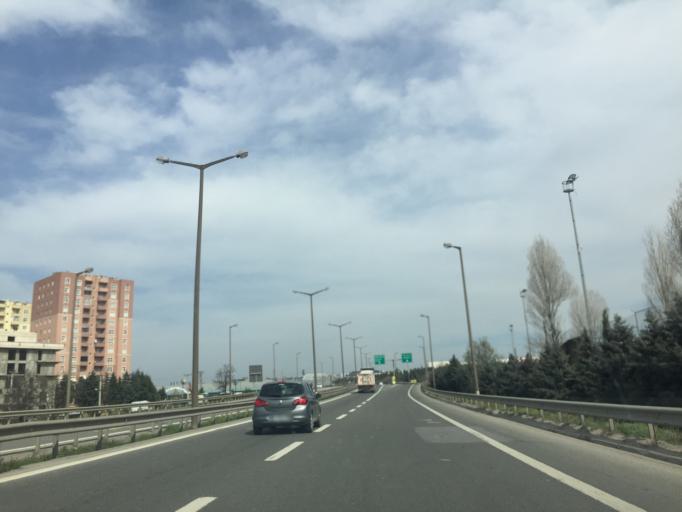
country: TR
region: Kocaeli
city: Balcik
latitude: 40.8687
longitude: 29.3923
